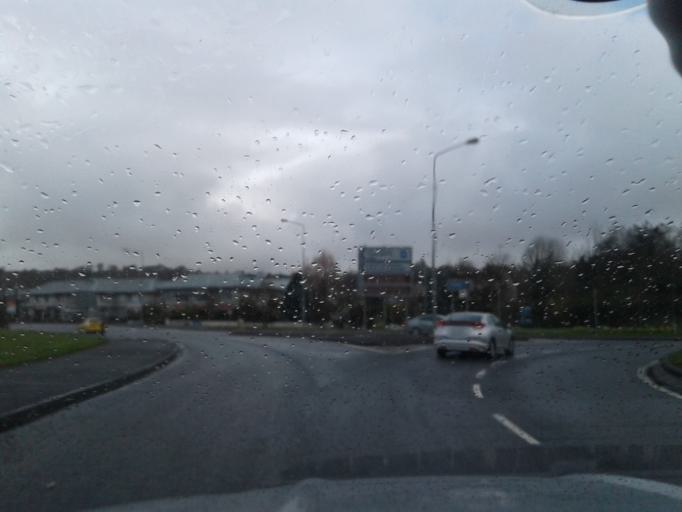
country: IE
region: Ulster
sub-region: County Donegal
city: Letterkenny
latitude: 54.9488
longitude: -7.7164
